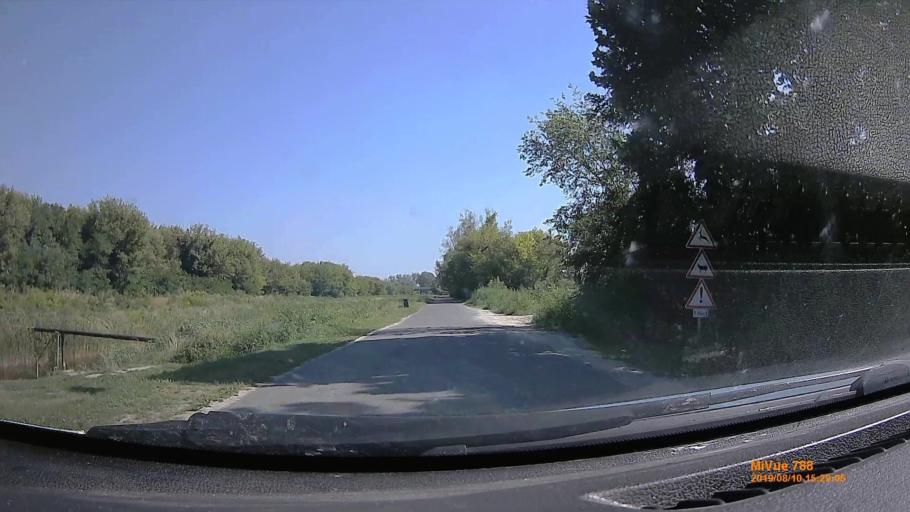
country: HU
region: Somogy
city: Balatonfenyves
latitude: 46.7076
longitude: 17.4804
